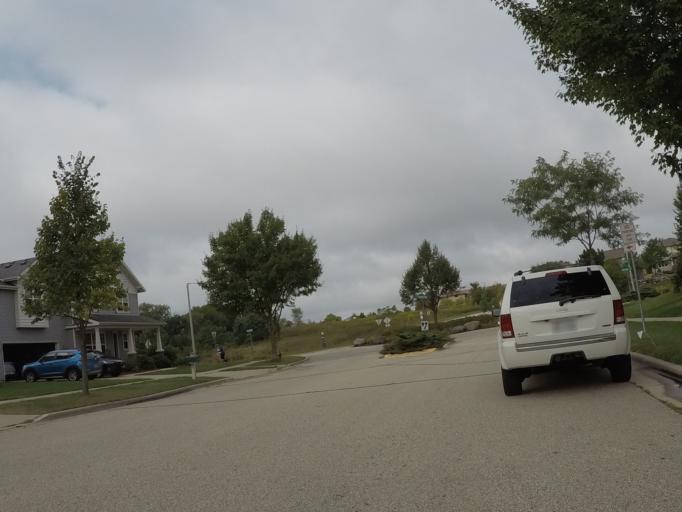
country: US
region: Wisconsin
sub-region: Dane County
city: Verona
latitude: 43.0432
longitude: -89.5414
